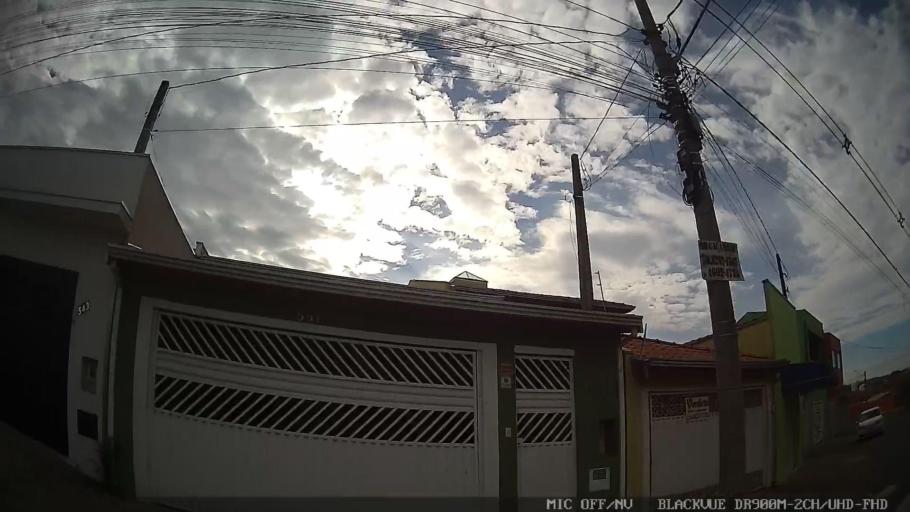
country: BR
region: Sao Paulo
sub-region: Salto
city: Salto
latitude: -23.1796
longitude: -47.2700
